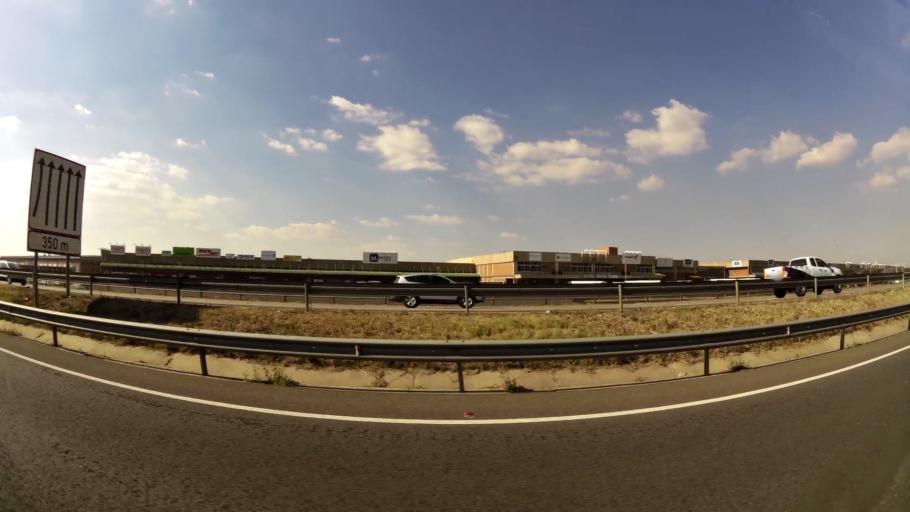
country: ZA
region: Gauteng
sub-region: City of Johannesburg Metropolitan Municipality
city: Modderfontein
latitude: -26.1086
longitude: 28.2401
